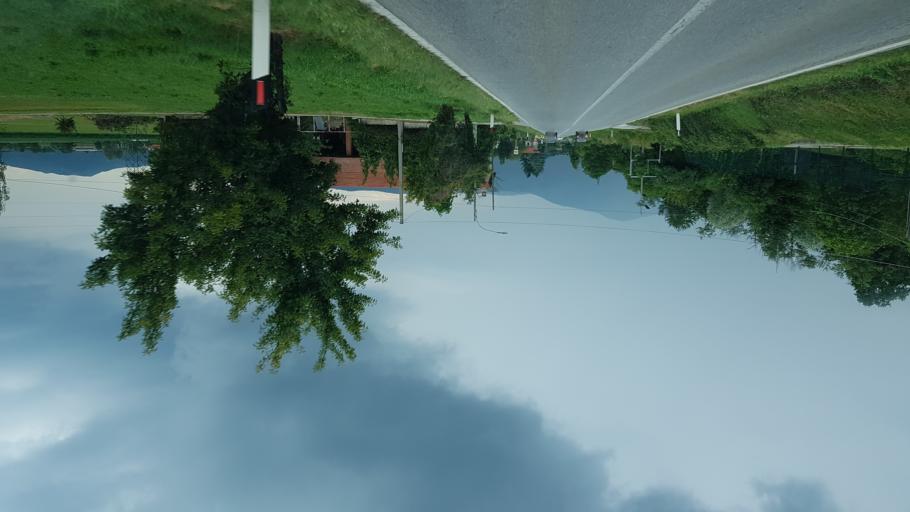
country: IT
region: Piedmont
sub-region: Provincia di Cuneo
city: Caraglio
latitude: 44.4284
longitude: 7.4255
